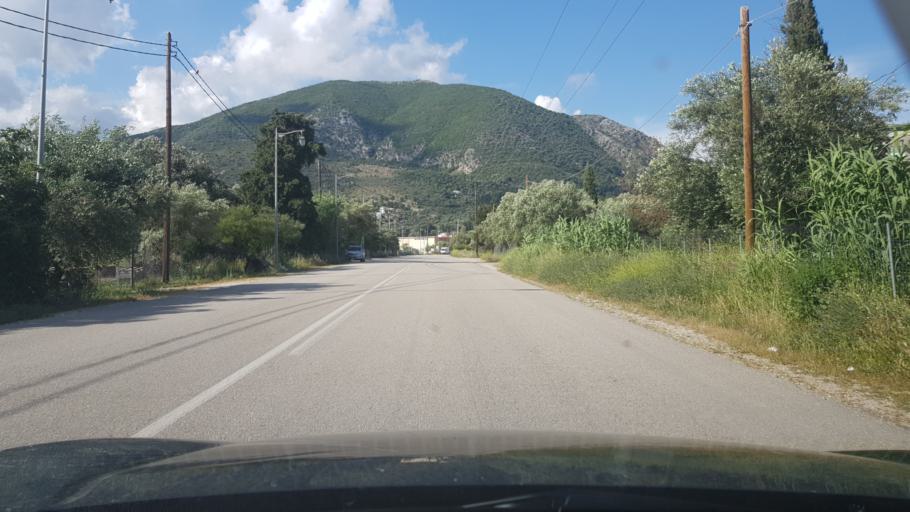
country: GR
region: Ionian Islands
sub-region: Lefkada
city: Nidri
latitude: 38.7066
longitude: 20.7040
